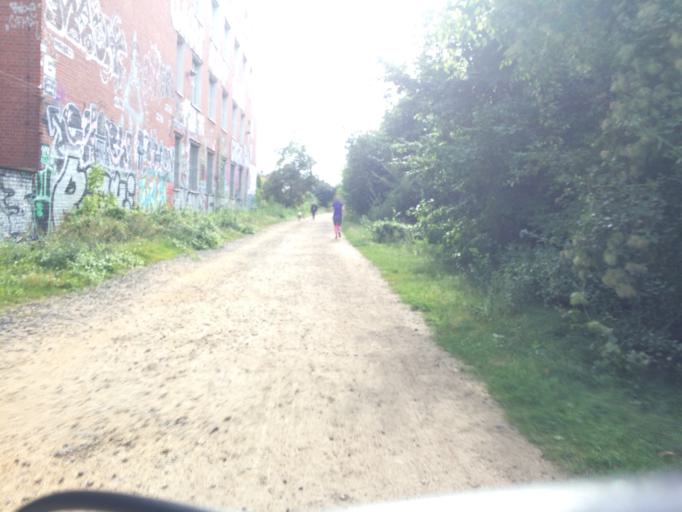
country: DE
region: Berlin
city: Berlin Treptow
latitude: 52.4935
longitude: 13.4467
